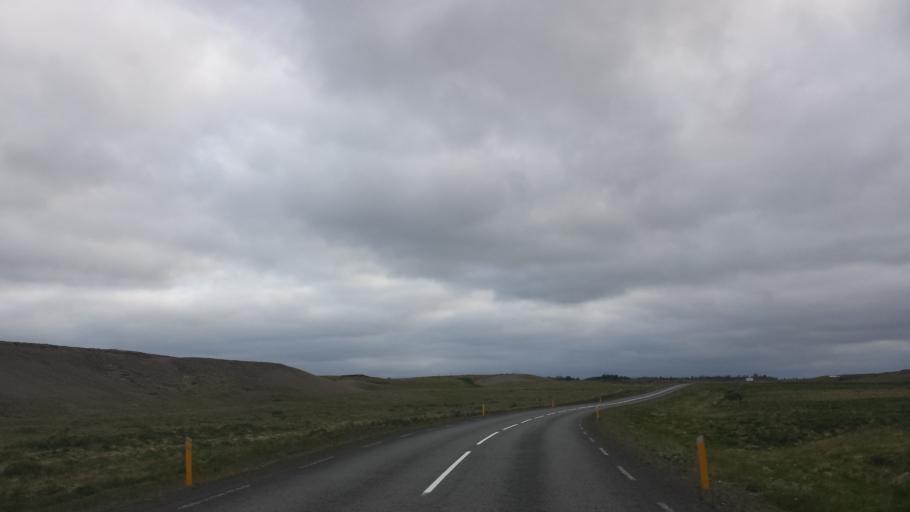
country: IS
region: South
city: Selfoss
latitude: 64.1251
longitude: -20.5946
